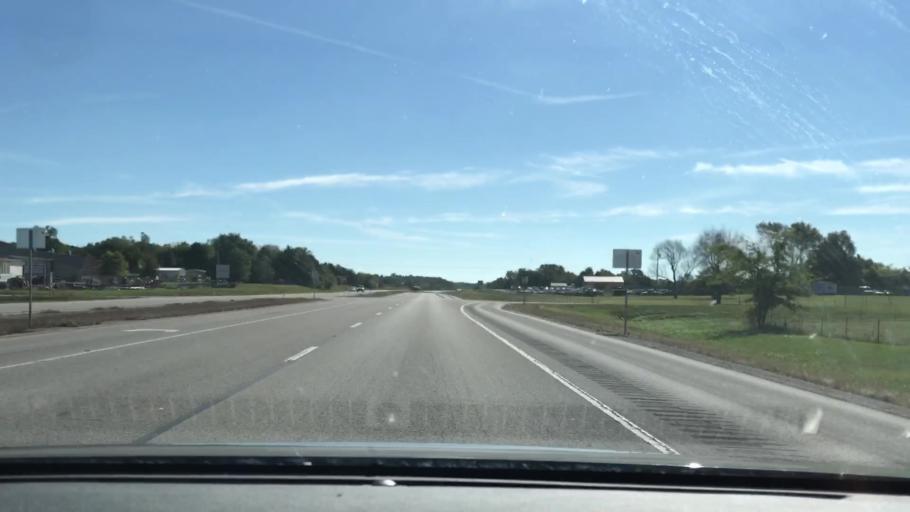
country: US
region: Kentucky
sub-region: Todd County
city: Elkton
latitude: 36.8368
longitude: -87.2390
